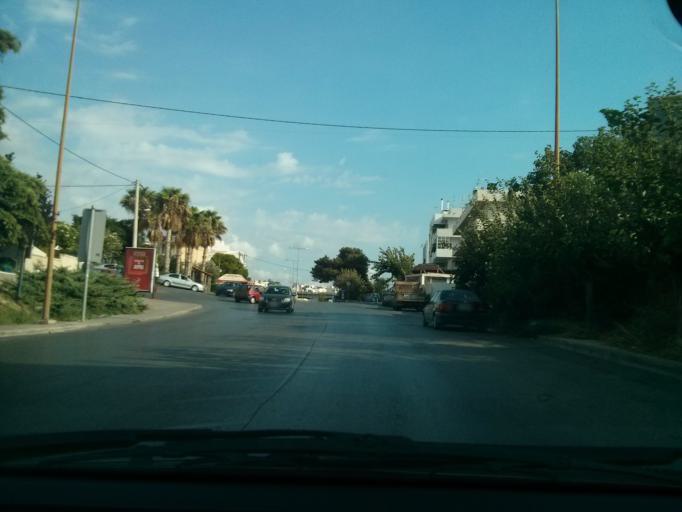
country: GR
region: Crete
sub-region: Nomos Irakleiou
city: Irakleion
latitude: 35.3239
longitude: 25.1405
